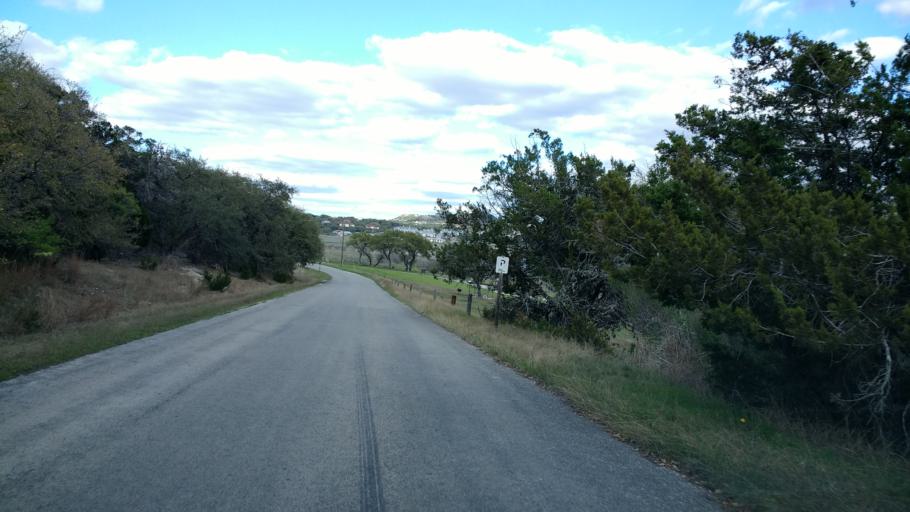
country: US
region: Texas
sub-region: Comal County
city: Canyon Lake
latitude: 29.9050
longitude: -98.2271
